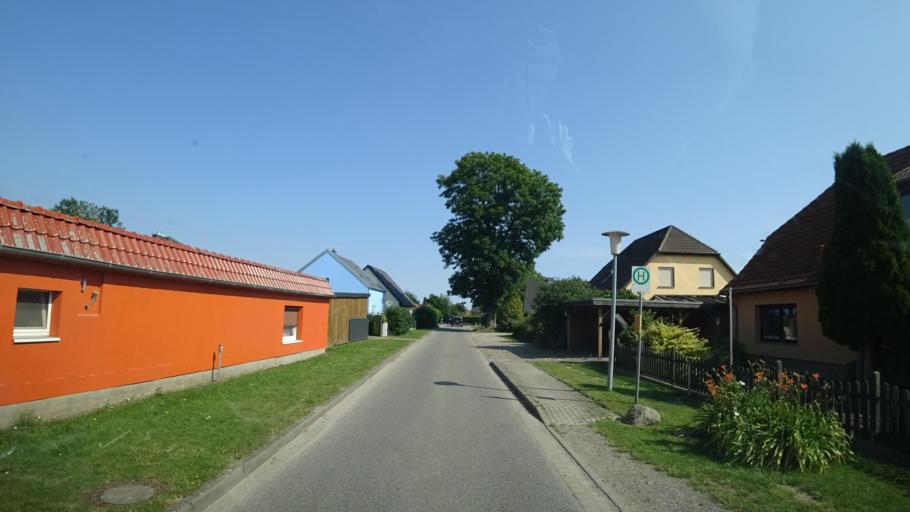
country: DE
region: Mecklenburg-Vorpommern
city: Kemnitz
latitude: 54.1126
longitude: 13.5319
